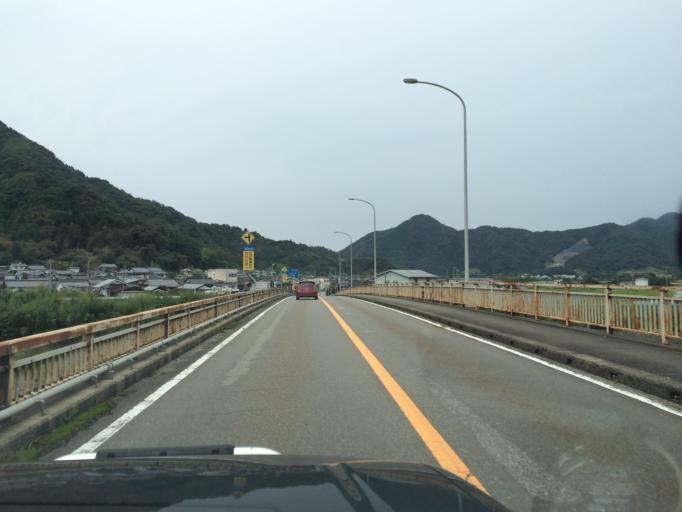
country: JP
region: Hyogo
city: Toyooka
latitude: 35.4186
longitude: 134.7916
